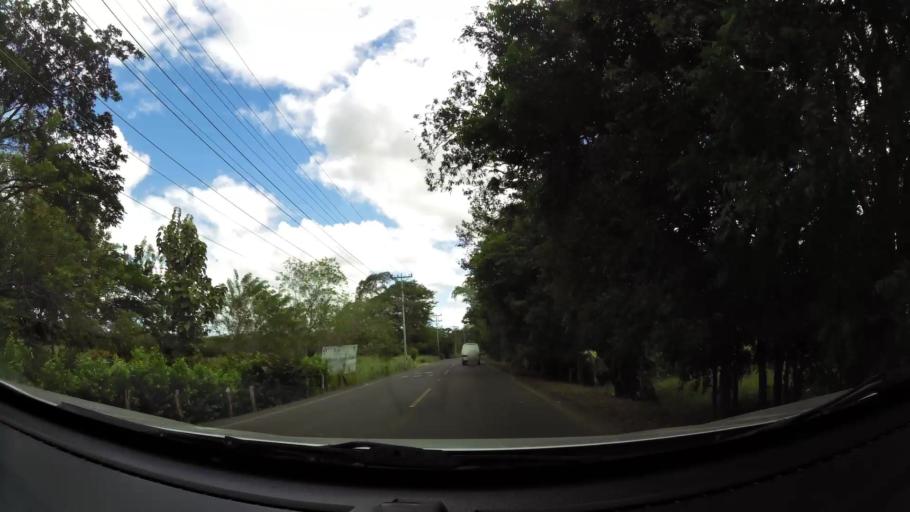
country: CR
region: Guanacaste
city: Santa Cruz
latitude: 10.2706
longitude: -85.5937
